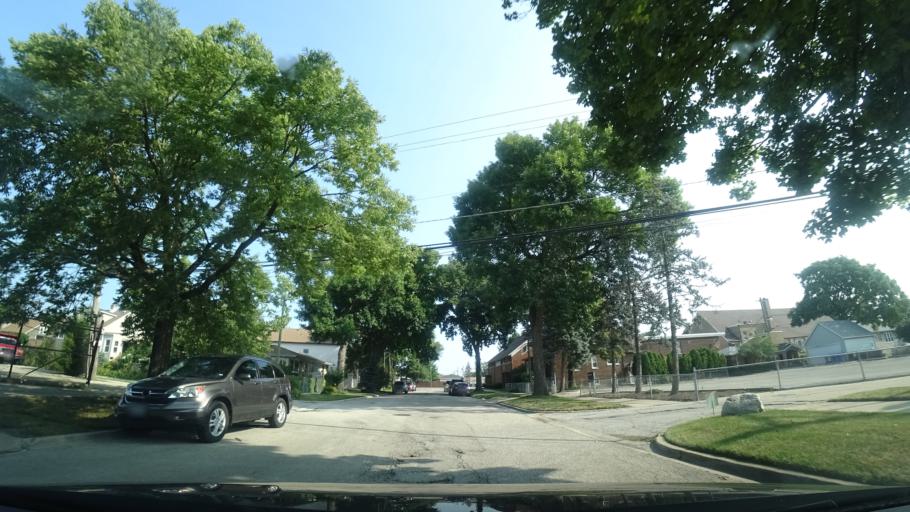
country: US
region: Illinois
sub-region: Cook County
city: Harwood Heights
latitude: 41.9748
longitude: -87.7821
